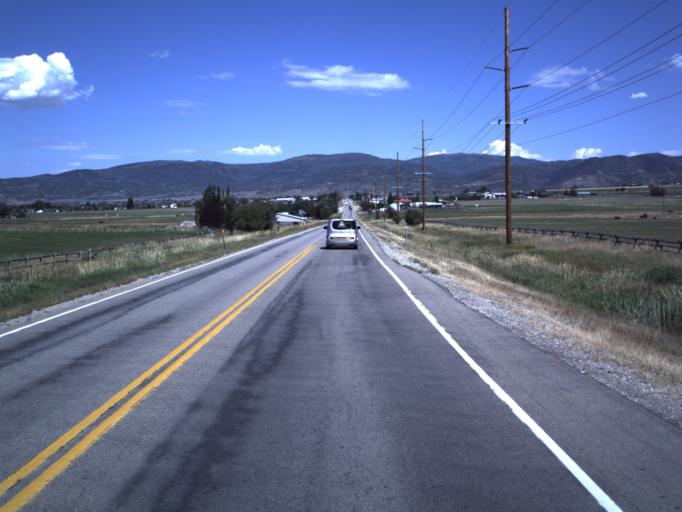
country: US
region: Utah
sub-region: Summit County
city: Kamas
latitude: 40.6610
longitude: -111.2808
